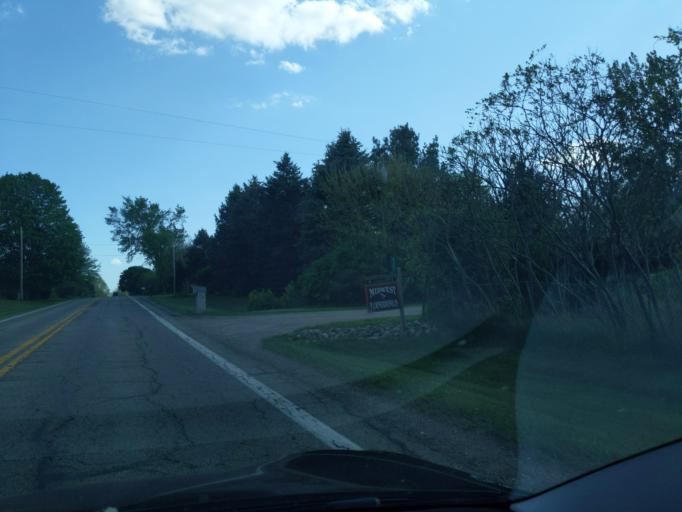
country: US
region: Michigan
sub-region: Eaton County
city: Potterville
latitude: 42.6887
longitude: -84.7396
